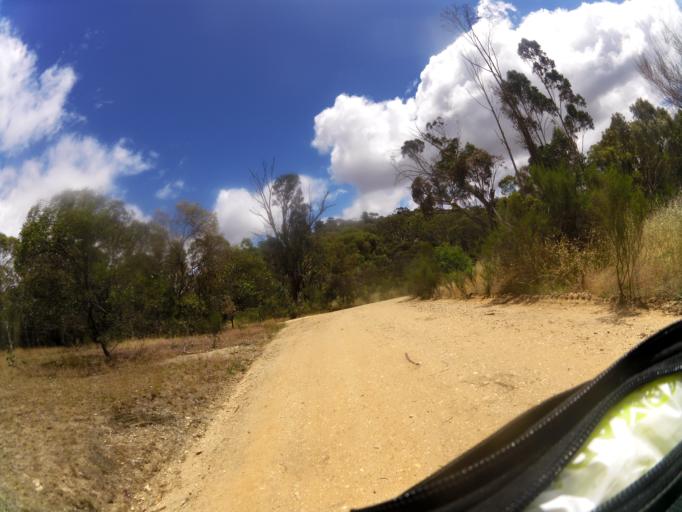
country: AU
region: Victoria
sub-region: Mount Alexander
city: Castlemaine
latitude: -37.0557
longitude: 144.2711
